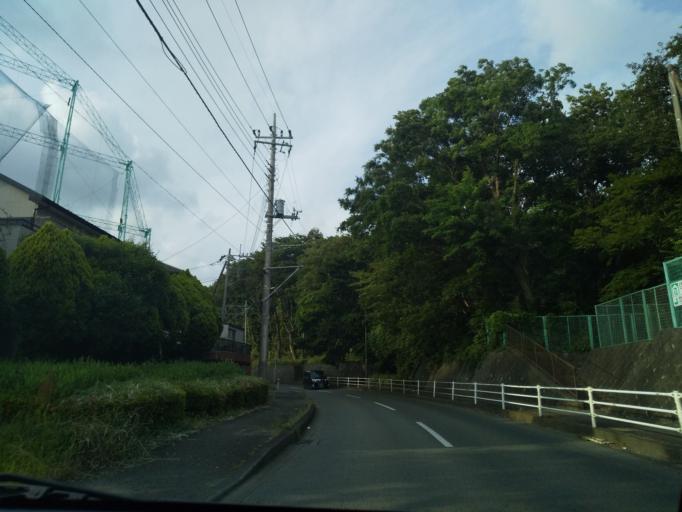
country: JP
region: Kanagawa
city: Zama
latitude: 35.5165
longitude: 139.3852
